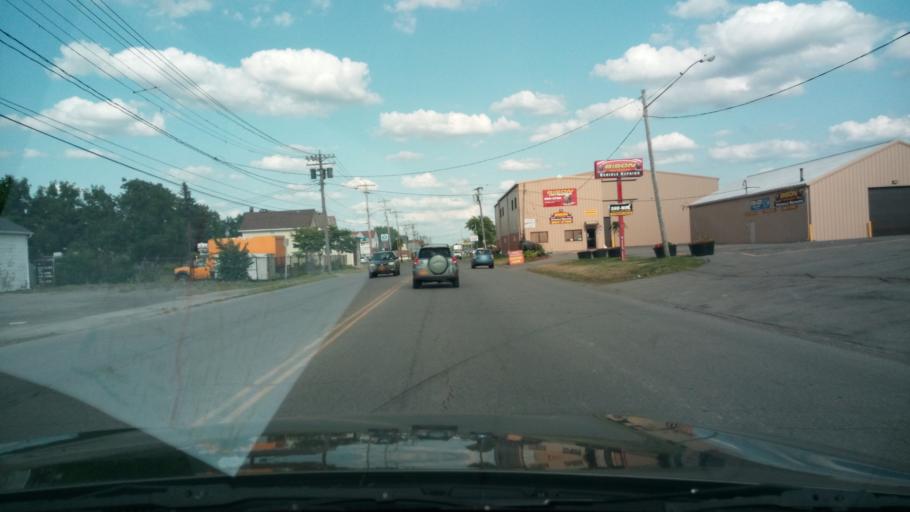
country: US
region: New York
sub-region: Erie County
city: Sloan
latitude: 42.8847
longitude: -78.8123
